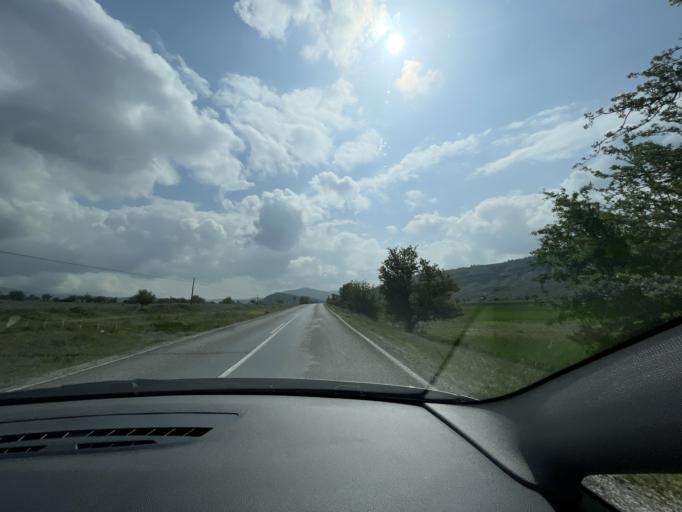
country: TR
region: Denizli
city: Acipayam
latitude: 37.5108
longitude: 29.4535
